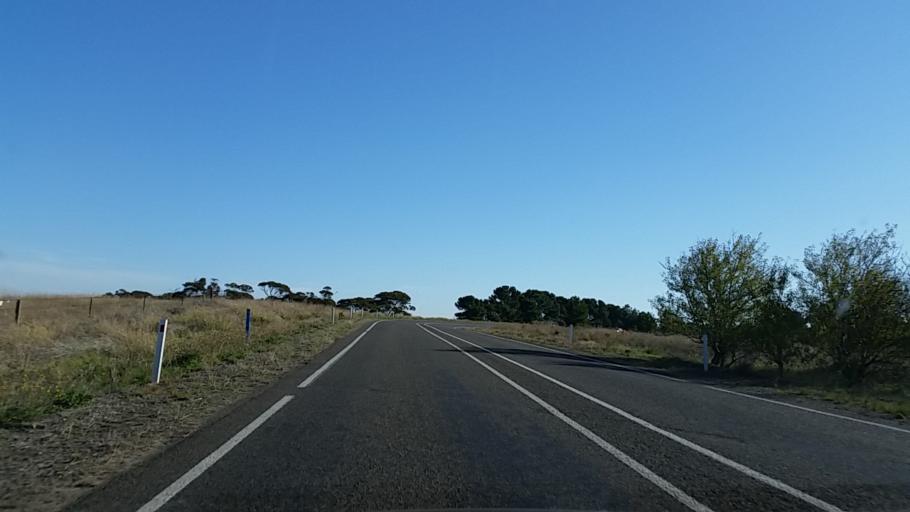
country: AU
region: South Australia
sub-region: Mount Barker
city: Callington
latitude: -35.1193
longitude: 139.1571
